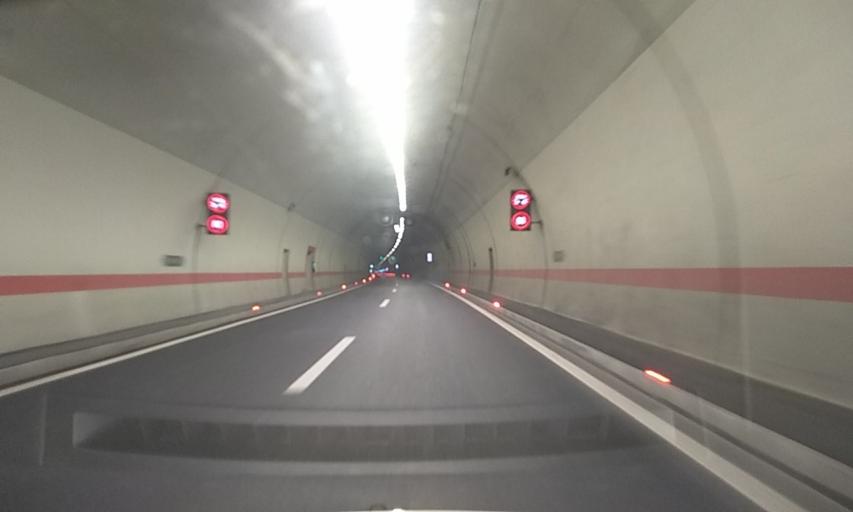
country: RS
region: Central Serbia
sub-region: Pcinjski Okrug
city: Vladicin Han
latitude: 42.7460
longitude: 22.0795
